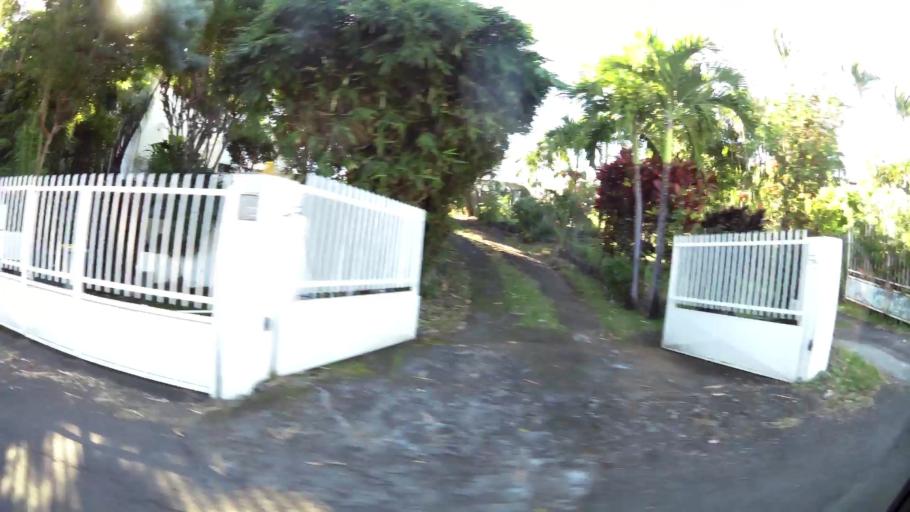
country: RE
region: Reunion
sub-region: Reunion
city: Saint-Denis
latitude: -20.9022
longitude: 55.4761
